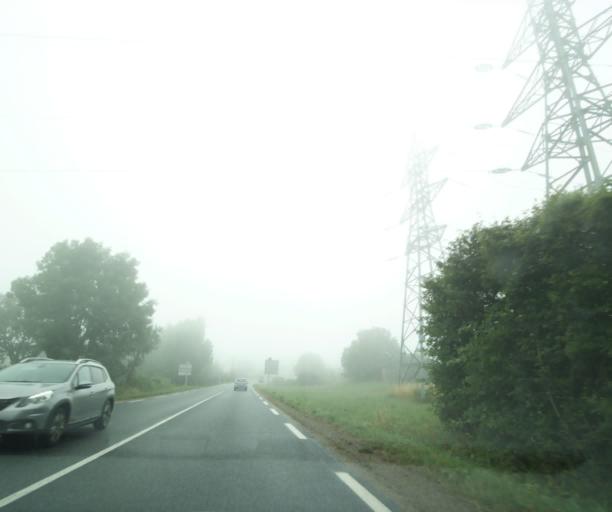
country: FR
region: Midi-Pyrenees
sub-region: Departement de l'Aveyron
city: Baraqueville
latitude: 44.2688
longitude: 2.4193
